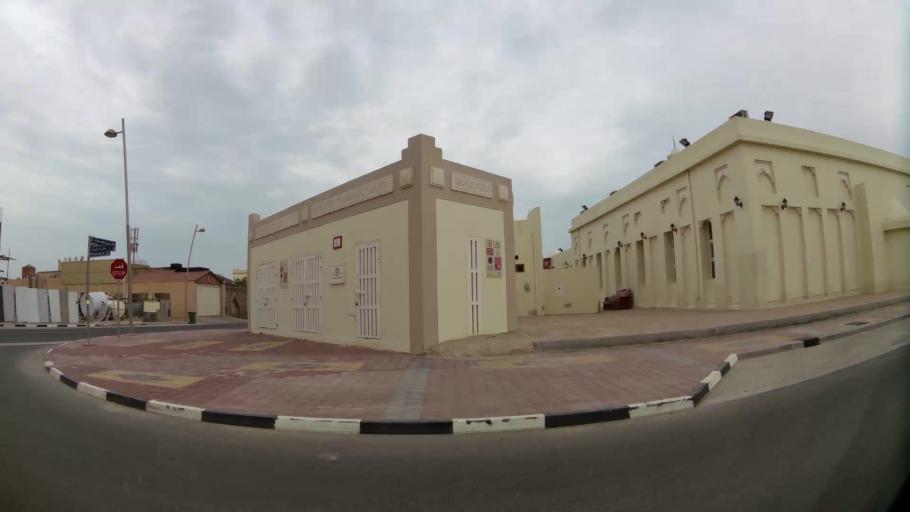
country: QA
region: Baladiyat ad Dawhah
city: Doha
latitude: 25.3437
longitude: 51.4832
